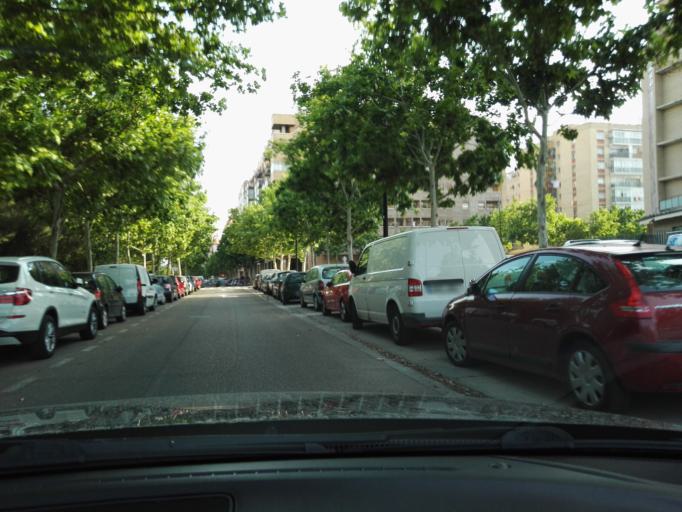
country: ES
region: Aragon
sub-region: Provincia de Zaragoza
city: Zaragoza
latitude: 41.6627
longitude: -0.8711
